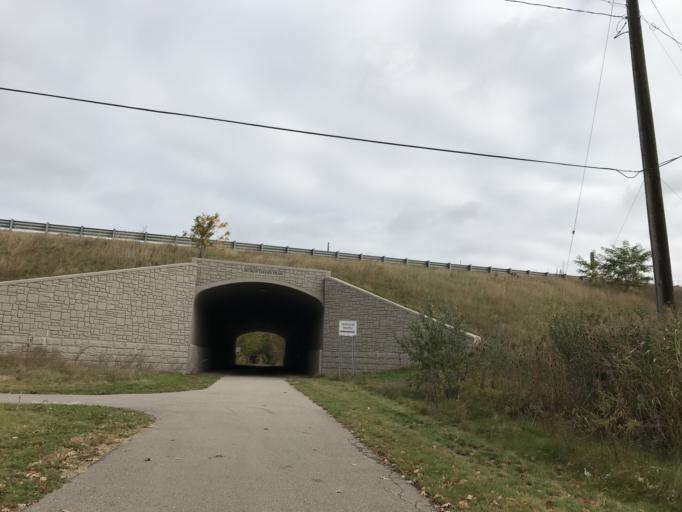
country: US
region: Michigan
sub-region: Oakland County
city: Wixom
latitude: 42.5156
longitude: -83.6062
